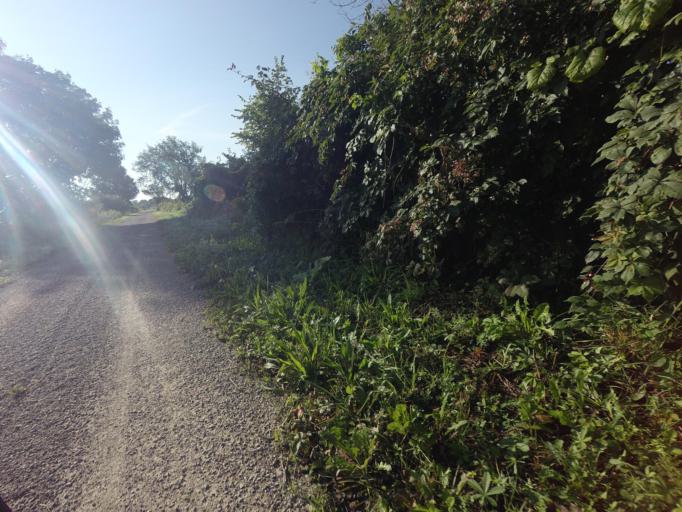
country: CA
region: Ontario
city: Goderich
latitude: 43.7544
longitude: -81.5105
